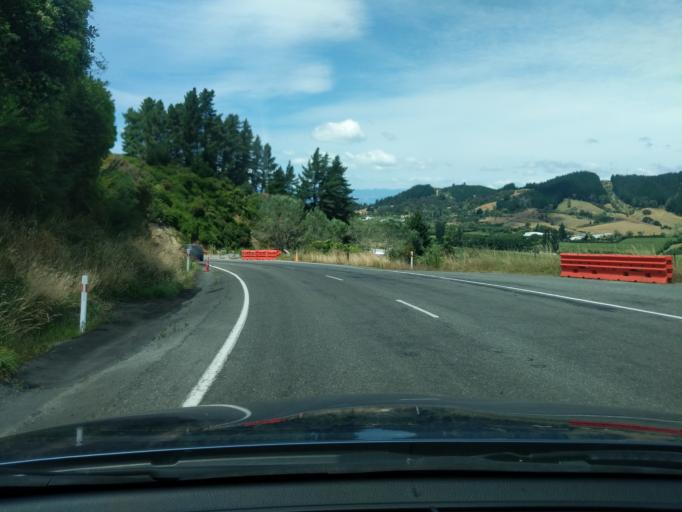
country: NZ
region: Tasman
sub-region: Tasman District
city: Motueka
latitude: -41.0506
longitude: 172.9608
